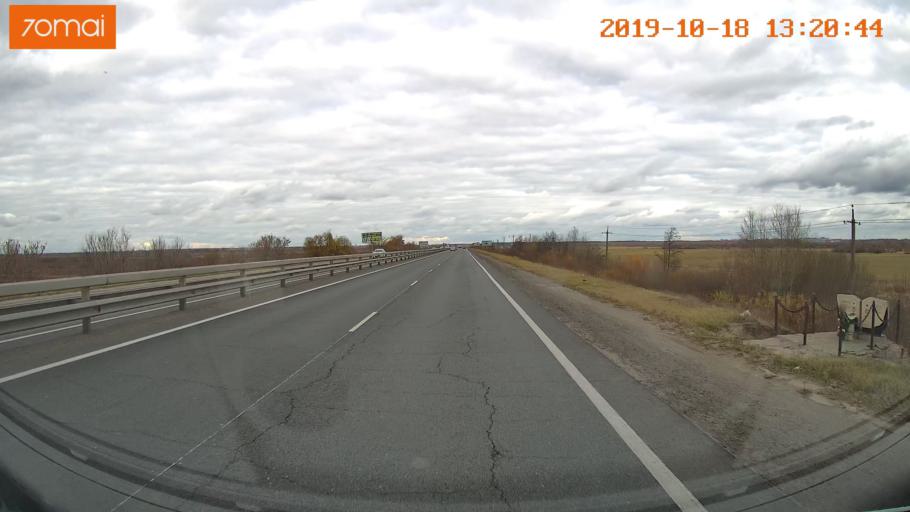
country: RU
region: Rjazan
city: Polyany
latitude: 54.6851
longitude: 39.8342
